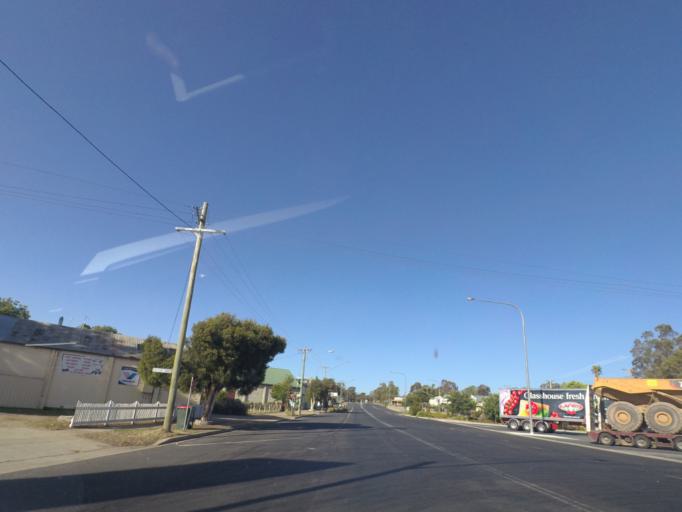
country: AU
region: New South Wales
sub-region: Wagga Wagga
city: Forest Hill
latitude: -35.2772
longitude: 147.7366
